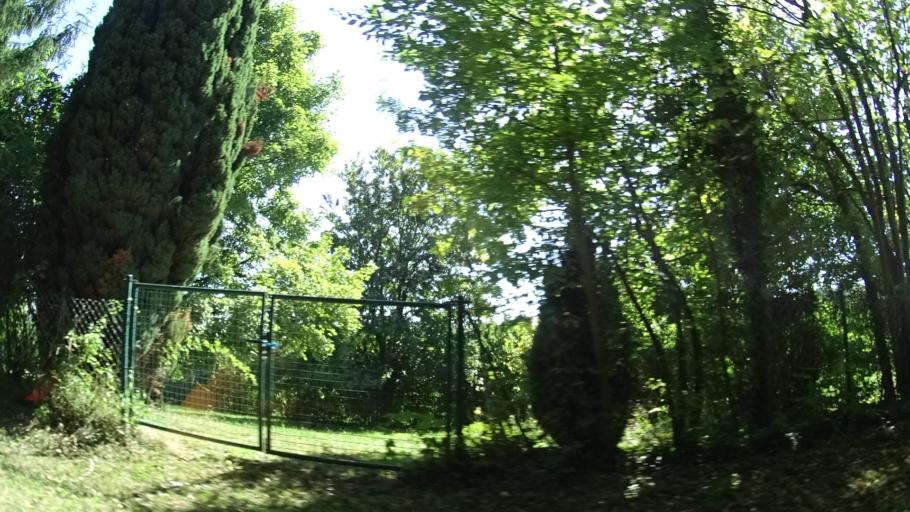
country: DE
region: Baden-Wuerttemberg
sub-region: Karlsruhe Region
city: Ubstadt-Weiher
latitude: 49.1319
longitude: 8.6534
